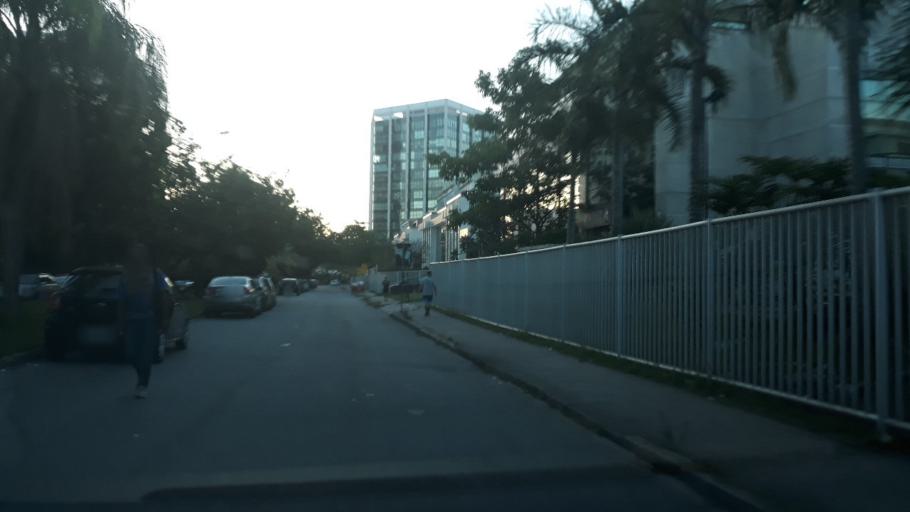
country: BR
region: Rio de Janeiro
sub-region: Rio De Janeiro
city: Rio de Janeiro
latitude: -23.0013
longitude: -43.3453
